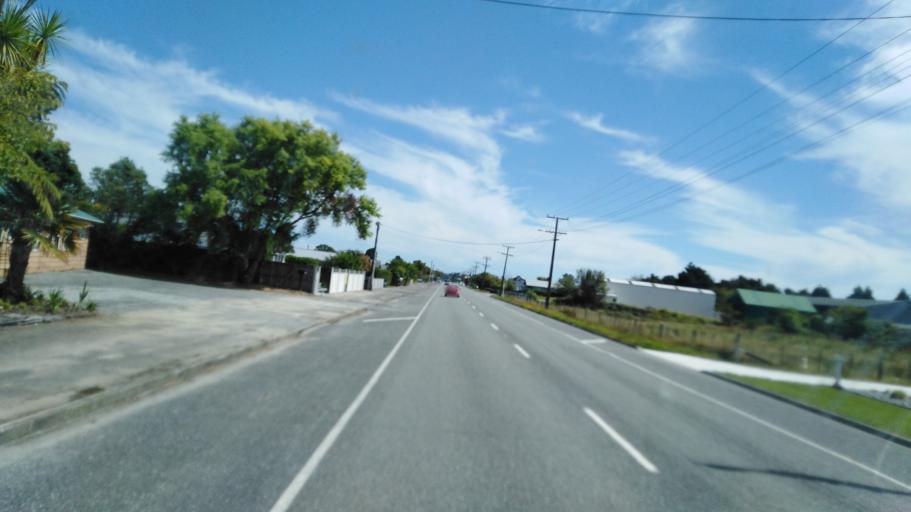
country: NZ
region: West Coast
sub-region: Buller District
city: Westport
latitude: -41.7532
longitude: 171.6167
